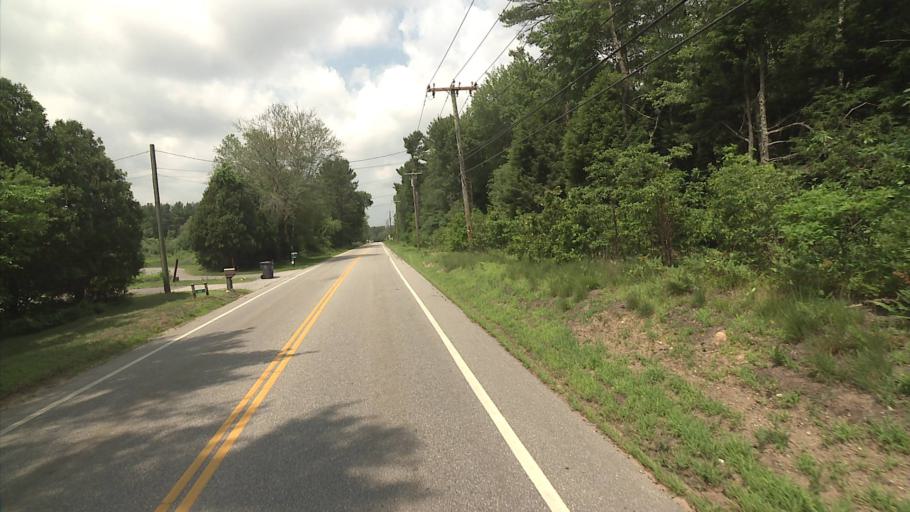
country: US
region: Connecticut
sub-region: Windham County
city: Plainfield
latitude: 41.5758
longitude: -71.8475
